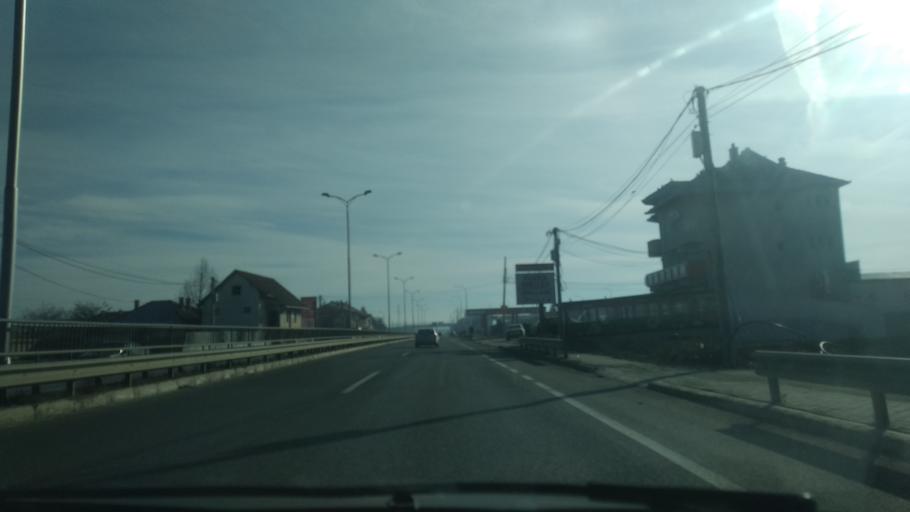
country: XK
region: Pristina
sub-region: Komuna e Obiliqit
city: Obiliq
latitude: 42.7206
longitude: 21.0878
